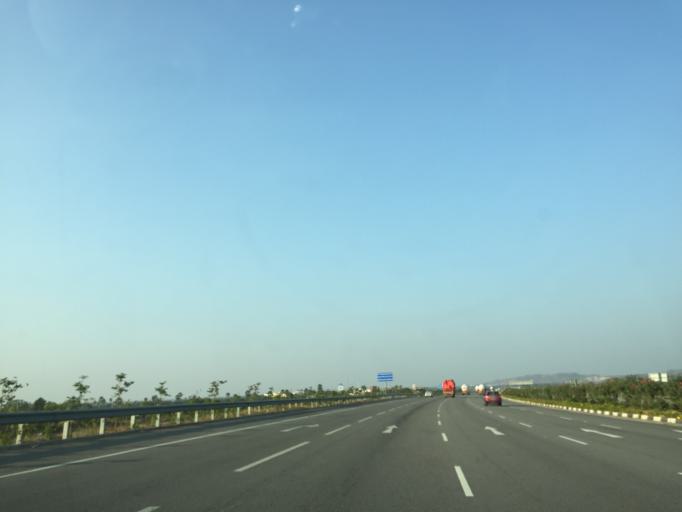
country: IN
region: Telangana
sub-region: Rangareddi
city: Ghatkesar
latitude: 17.4480
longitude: 78.6677
